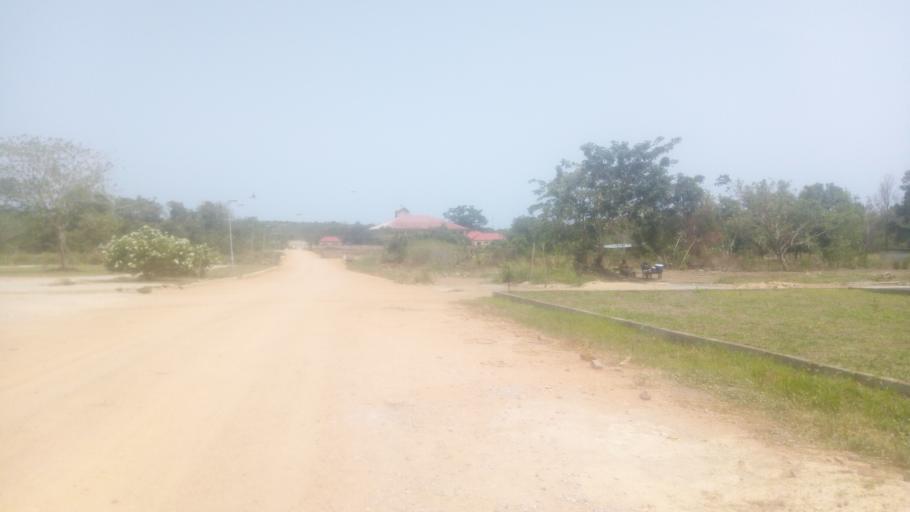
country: GH
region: Central
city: Winneba
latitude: 5.3699
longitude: -0.6317
